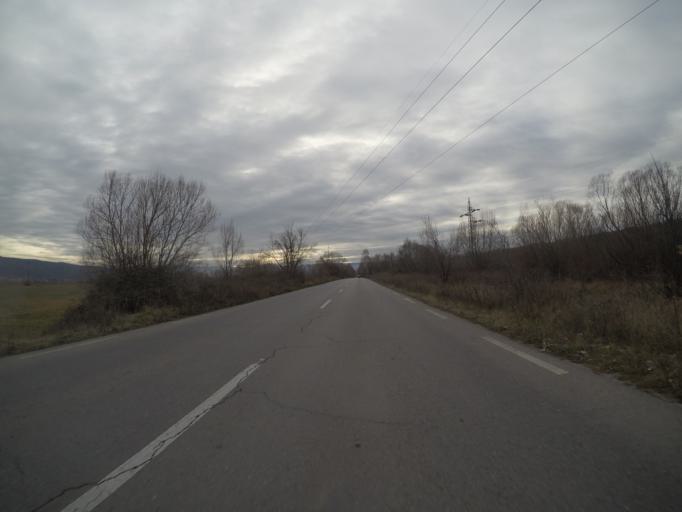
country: BG
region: Kyustendil
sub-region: Obshtina Rila
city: Rila
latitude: 42.1100
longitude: 23.1058
